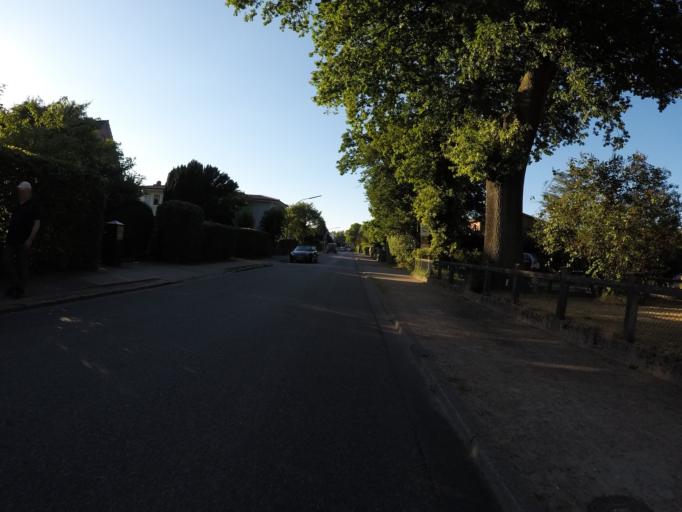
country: DE
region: Hamburg
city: Duvenstedt
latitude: 53.7044
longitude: 10.1107
